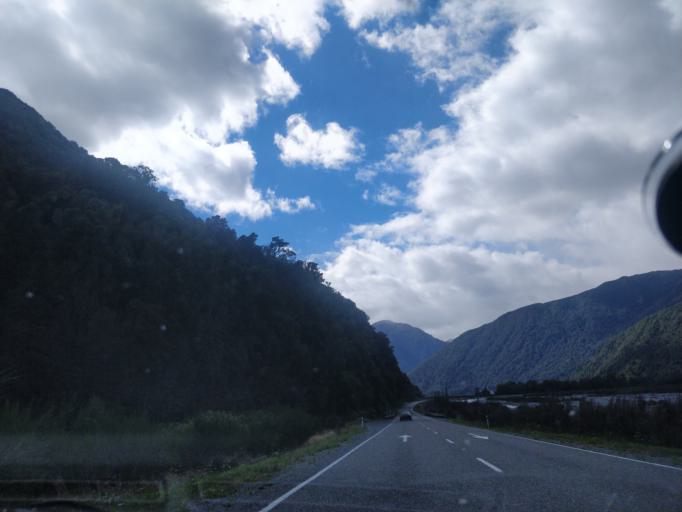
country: NZ
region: West Coast
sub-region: Grey District
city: Greymouth
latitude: -42.7938
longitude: 171.5912
